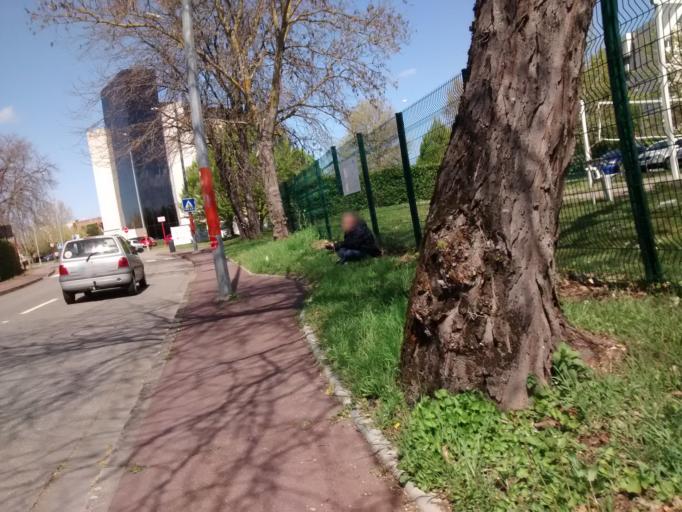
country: FR
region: Midi-Pyrenees
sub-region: Departement de la Haute-Garonne
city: Labege
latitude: 43.5390
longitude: 1.5159
